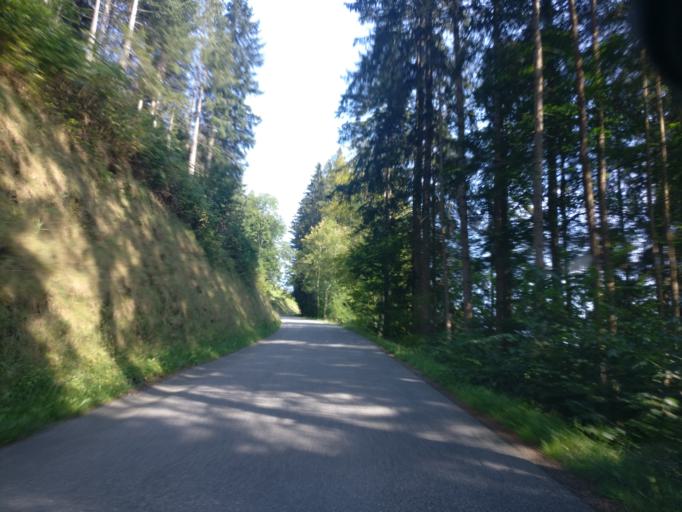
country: AT
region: Salzburg
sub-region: Politischer Bezirk Sankt Johann im Pongau
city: Pfarrwerfen
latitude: 47.4648
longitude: 13.2111
